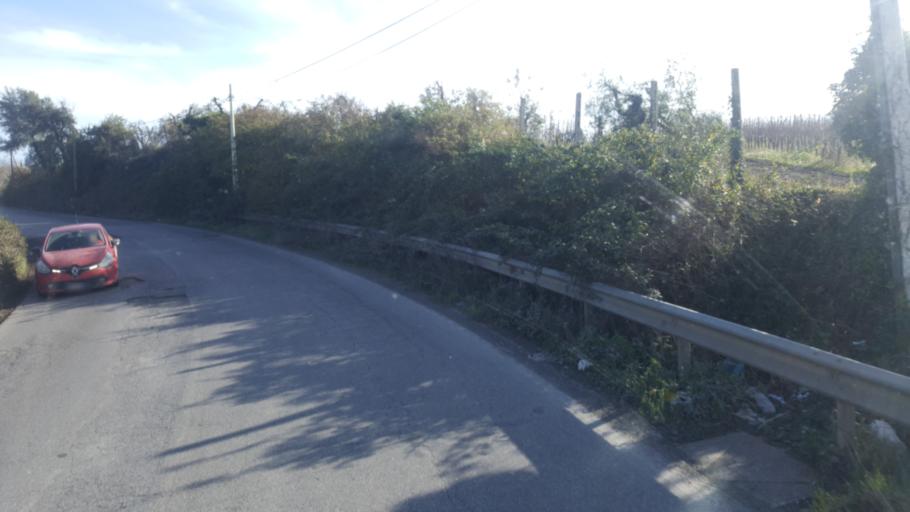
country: IT
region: Latium
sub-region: Citta metropolitana di Roma Capitale
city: Mantiglia di Ardea
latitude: 41.6881
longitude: 12.6040
